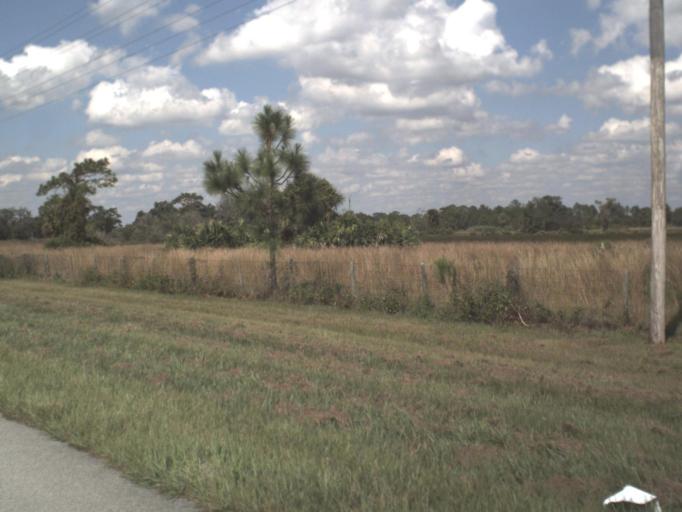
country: US
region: Florida
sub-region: Okeechobee County
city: Okeechobee
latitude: 27.3853
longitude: -81.0034
